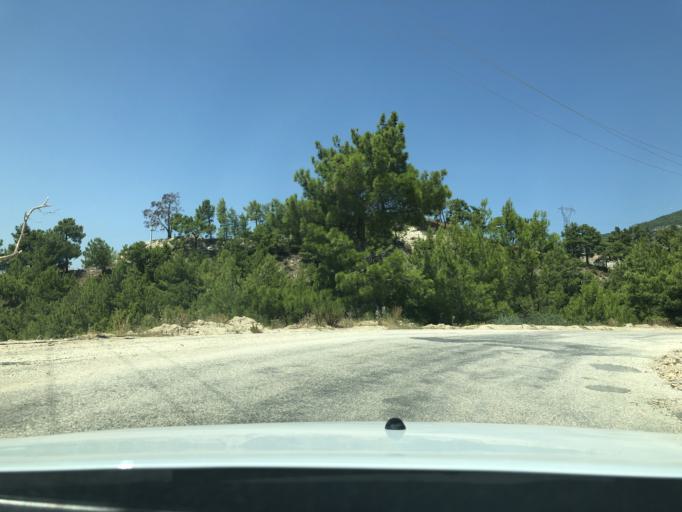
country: TR
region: Antalya
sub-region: Manavgat
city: Manavgat
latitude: 36.8695
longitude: 31.5557
